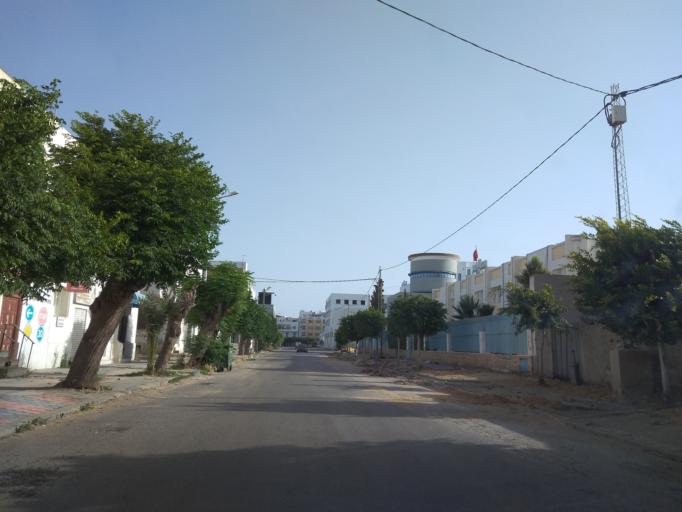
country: TN
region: Safaqis
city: Sfax
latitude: 34.7307
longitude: 10.7573
